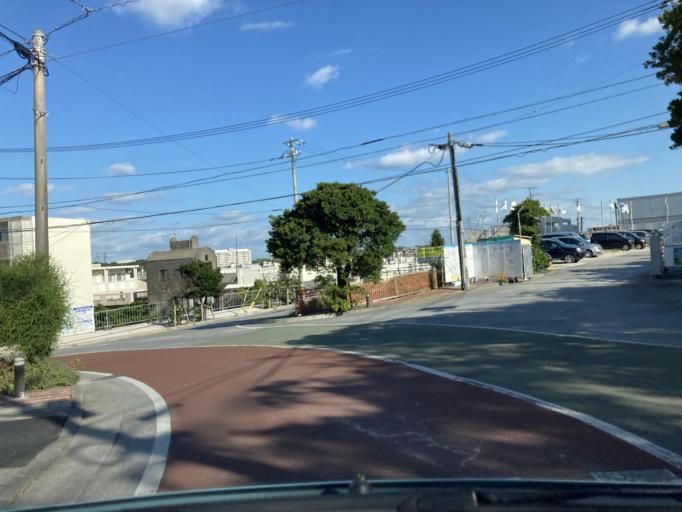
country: JP
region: Okinawa
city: Ginowan
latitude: 26.2278
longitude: 127.7327
